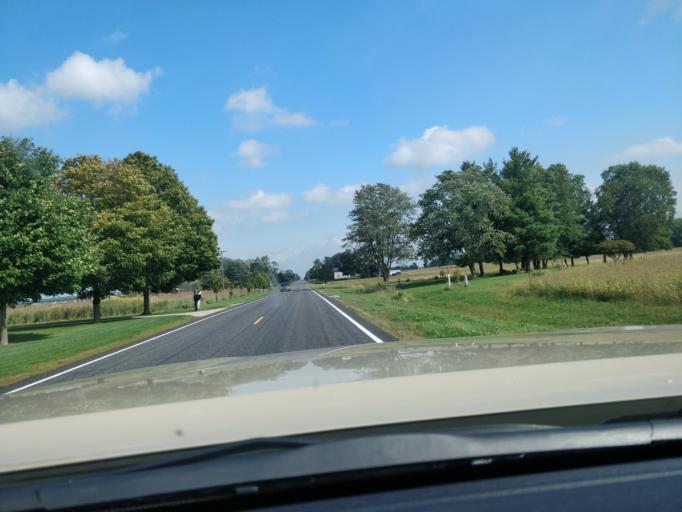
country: US
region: Michigan
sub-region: Ionia County
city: Saranac
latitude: 42.8861
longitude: -85.1615
